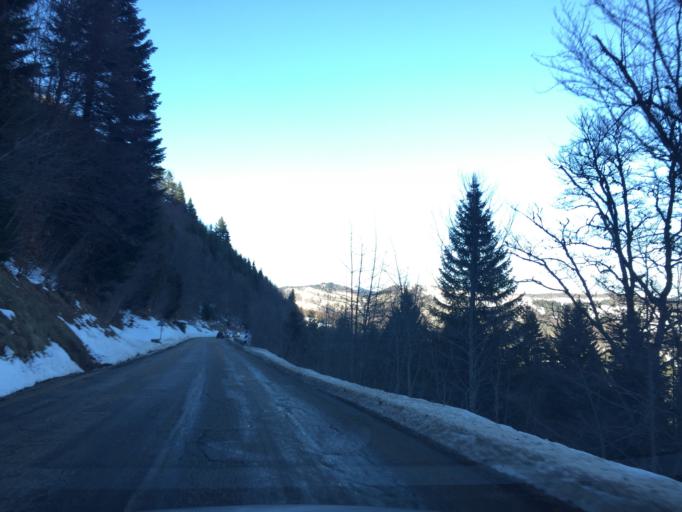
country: FR
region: Rhone-Alpes
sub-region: Departement de la Savoie
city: Mouxy
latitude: 45.6845
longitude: 5.9969
